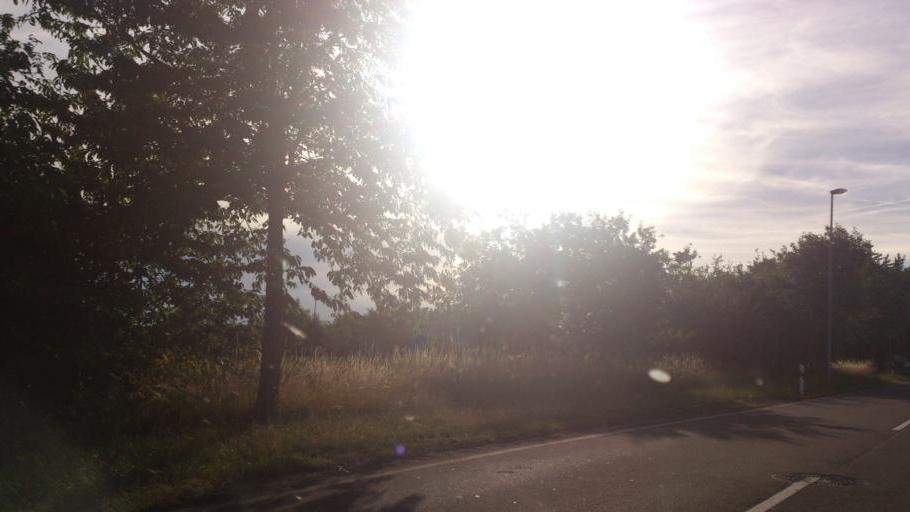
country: DE
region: Saarland
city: Bexbach
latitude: 49.3722
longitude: 7.2676
